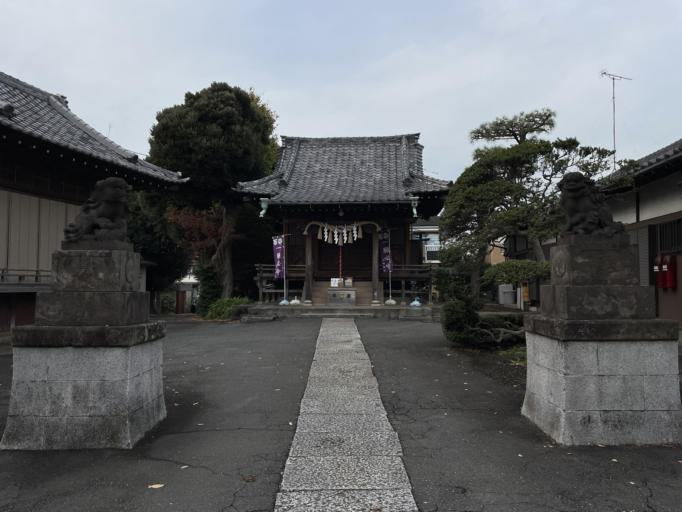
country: JP
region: Kanagawa
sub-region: Kawasaki-shi
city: Kawasaki
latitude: 35.5791
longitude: 139.7112
